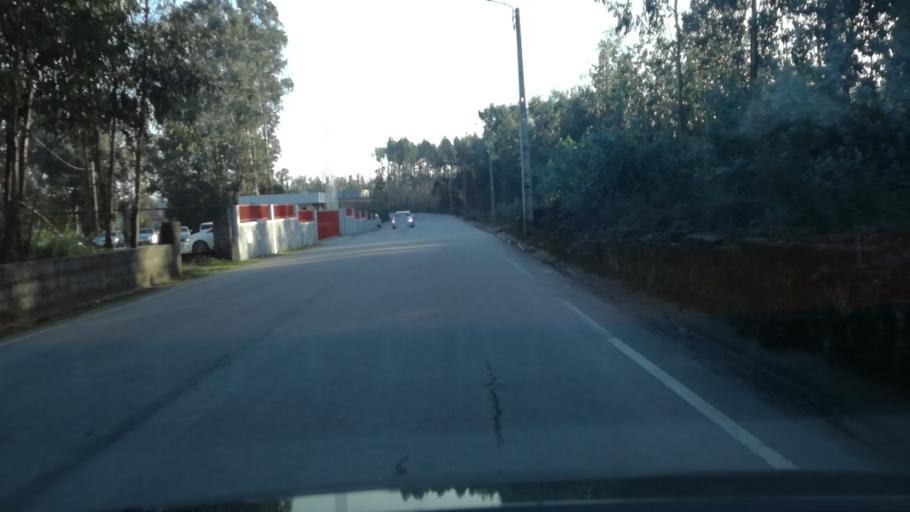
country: PT
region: Braga
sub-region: Vila Nova de Famalicao
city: Ferreiros
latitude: 41.3641
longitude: -8.5329
